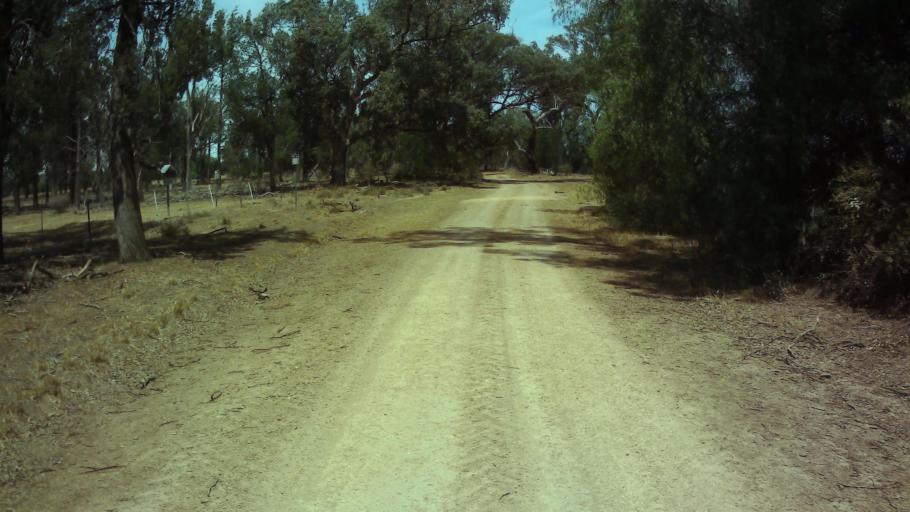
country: AU
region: New South Wales
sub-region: Weddin
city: Grenfell
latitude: -34.0308
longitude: 147.9342
